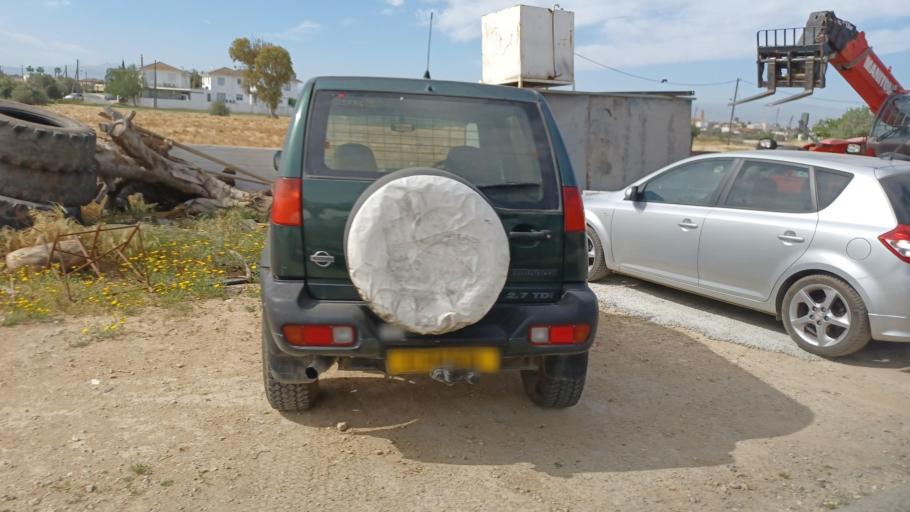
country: CY
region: Lefkosia
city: Kokkinotrimithia
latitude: 35.1583
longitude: 33.2032
